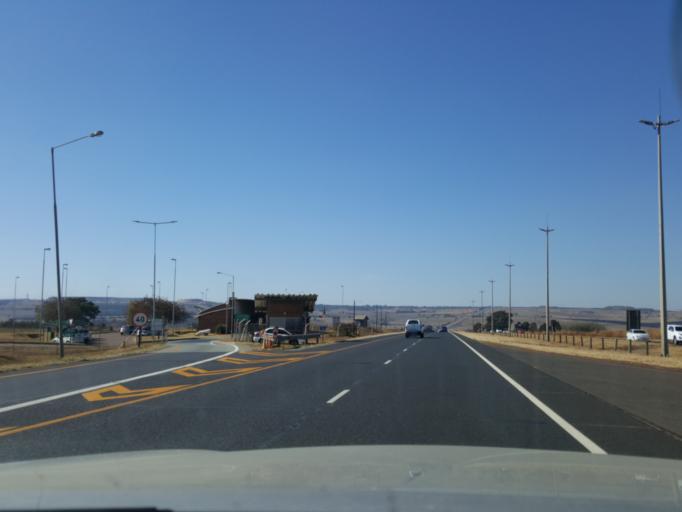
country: ZA
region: Mpumalanga
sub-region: Nkangala District Municipality
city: Middelburg
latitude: -25.8644
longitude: 29.3663
